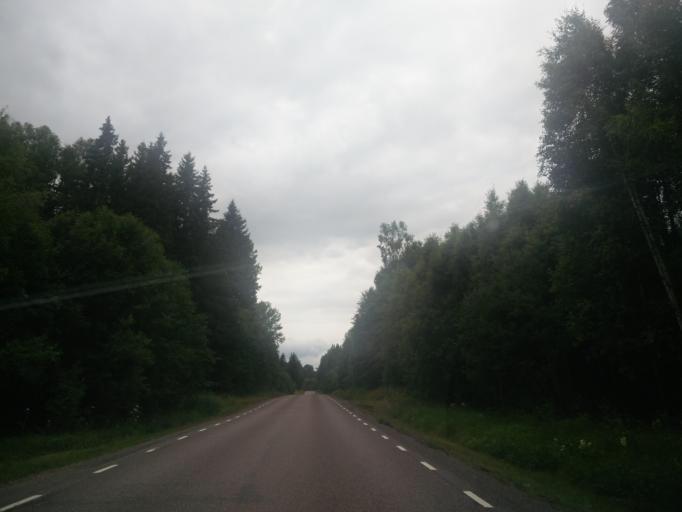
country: SE
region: Vaermland
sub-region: Arvika Kommun
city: Arvika
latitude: 59.9527
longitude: 12.7304
